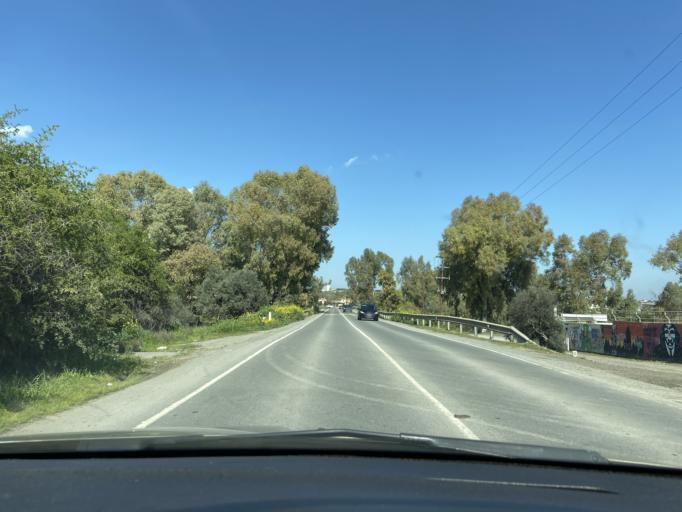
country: CY
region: Lefkosia
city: Dali
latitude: 35.0182
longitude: 33.3949
